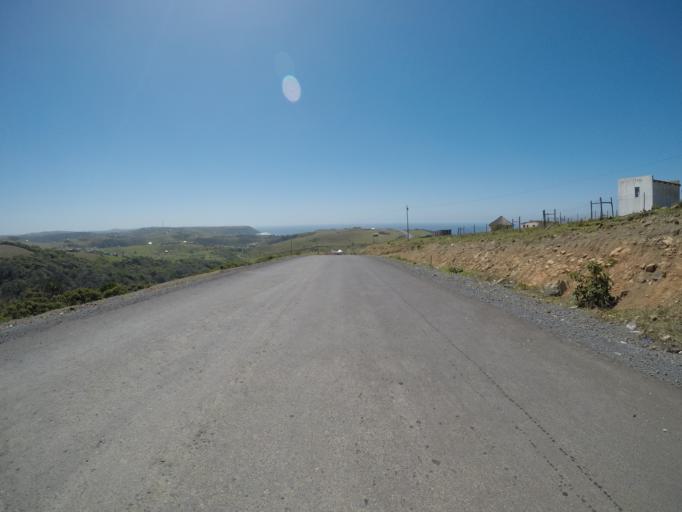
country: ZA
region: Eastern Cape
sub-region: OR Tambo District Municipality
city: Libode
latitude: -31.9930
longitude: 29.1339
